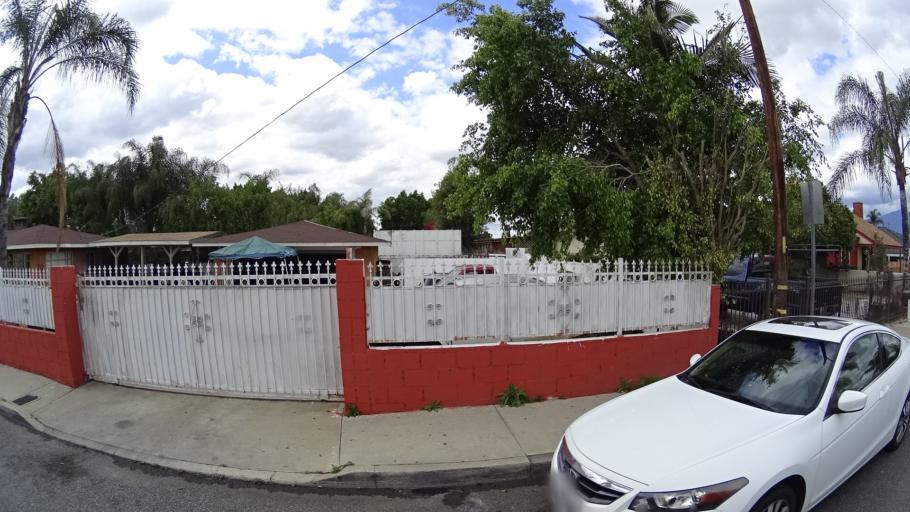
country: US
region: California
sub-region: Los Angeles County
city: Baldwin Park
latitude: 34.1001
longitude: -117.9523
